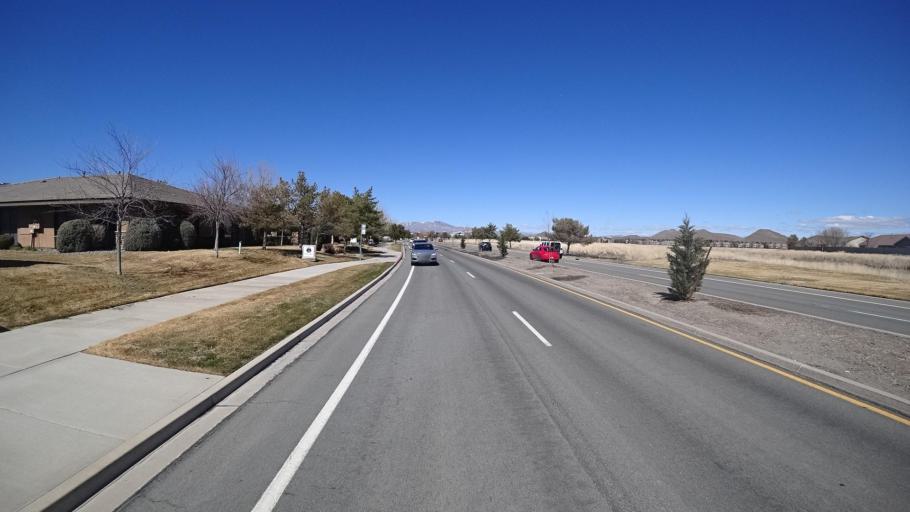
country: US
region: Nevada
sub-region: Washoe County
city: Sparks
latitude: 39.4302
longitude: -119.7535
